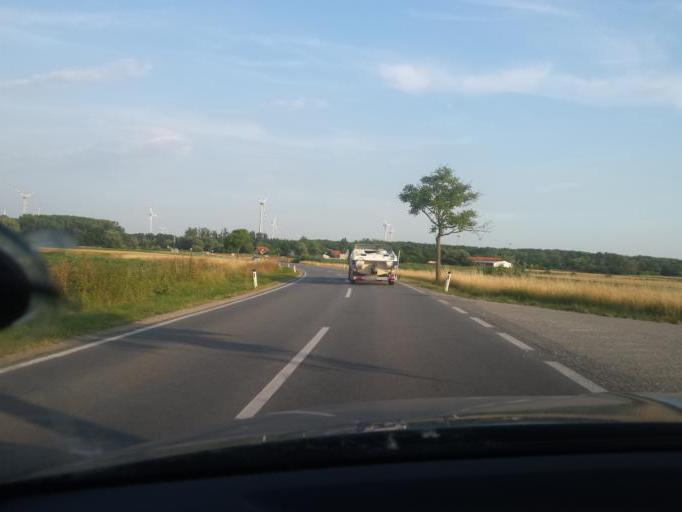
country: AT
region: Lower Austria
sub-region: Politischer Bezirk Bruck an der Leitha
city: Rohrau
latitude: 48.0736
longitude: 16.8609
